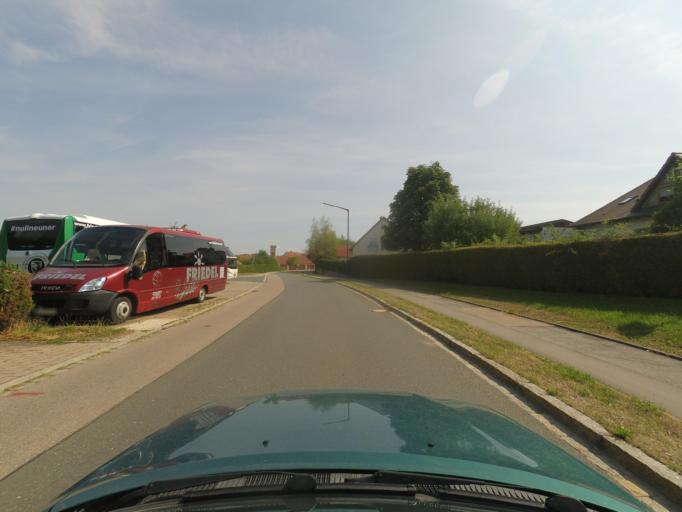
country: DE
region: Bavaria
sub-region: Regierungsbezirk Mittelfranken
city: Arberg
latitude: 49.1449
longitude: 10.6212
